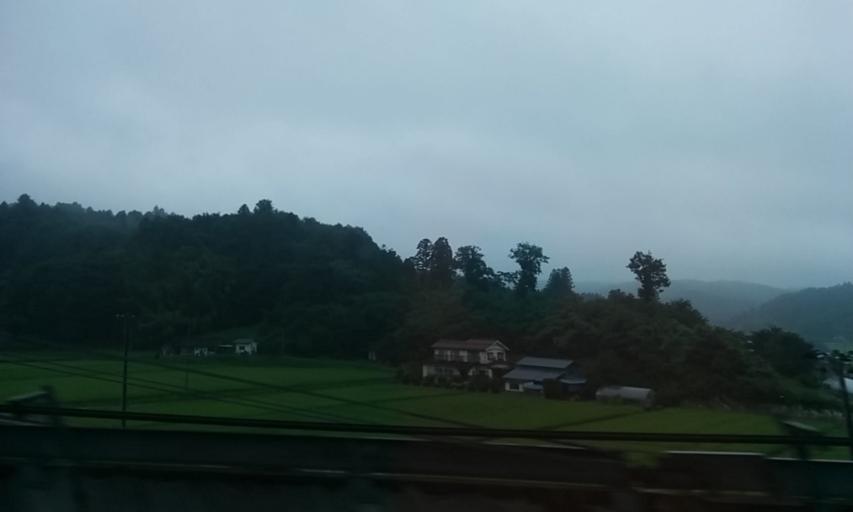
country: JP
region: Miyagi
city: Okawara
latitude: 38.0492
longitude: 140.6982
